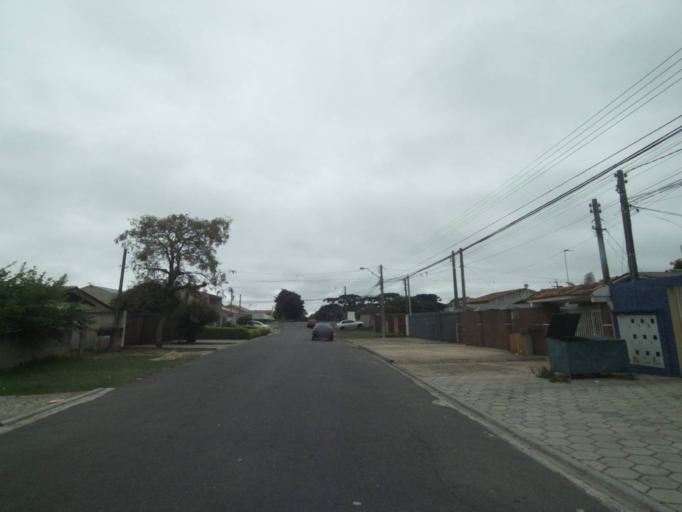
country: BR
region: Parana
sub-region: Sao Jose Dos Pinhais
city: Sao Jose dos Pinhais
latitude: -25.5450
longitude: -49.2819
